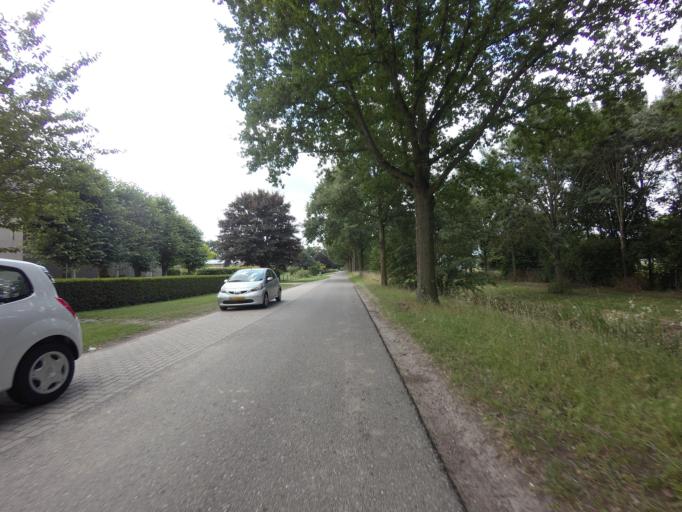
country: NL
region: Utrecht
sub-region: Gemeente Utrecht
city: Lunetten
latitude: 52.0362
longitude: 5.1243
